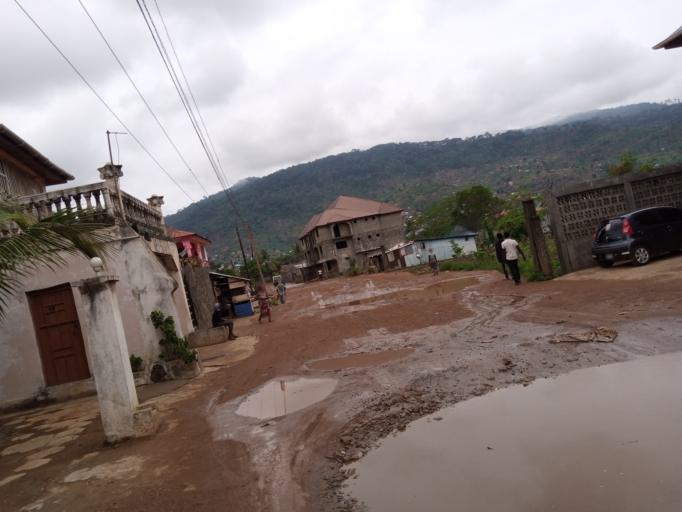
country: SL
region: Western Area
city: Hastings
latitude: 8.3815
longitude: -13.1498
